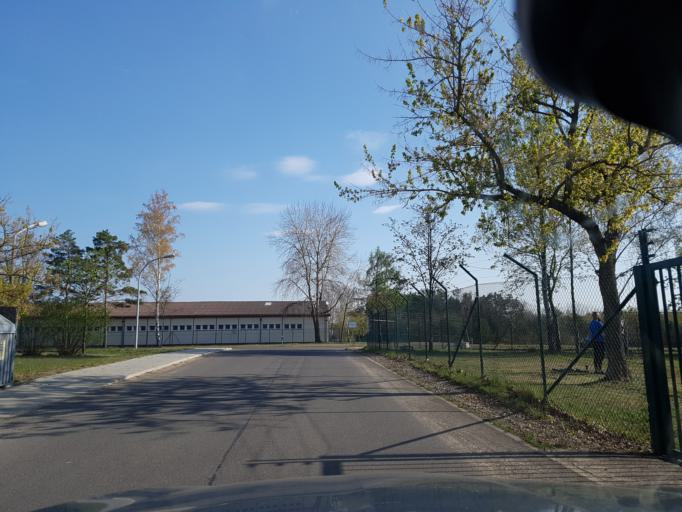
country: DE
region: Brandenburg
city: Schonborn
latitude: 51.6300
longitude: 13.5162
